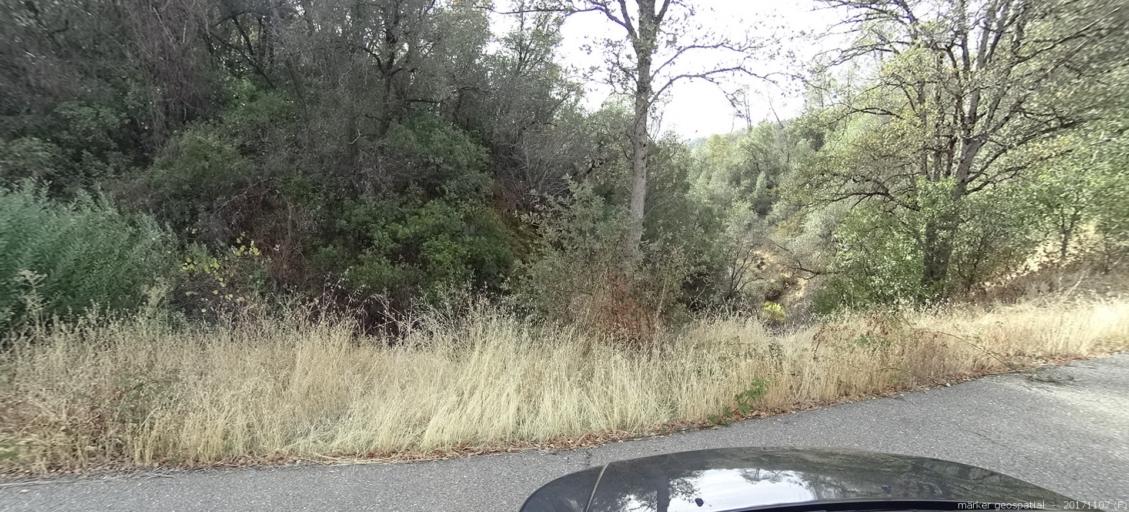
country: US
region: California
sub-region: Shasta County
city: Shasta
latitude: 40.5417
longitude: -122.5268
